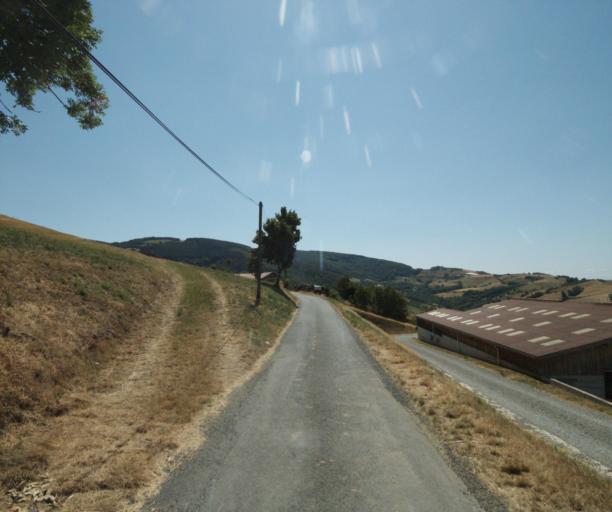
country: FR
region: Rhone-Alpes
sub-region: Departement du Rhone
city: Courzieu
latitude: 45.7457
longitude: 4.5804
